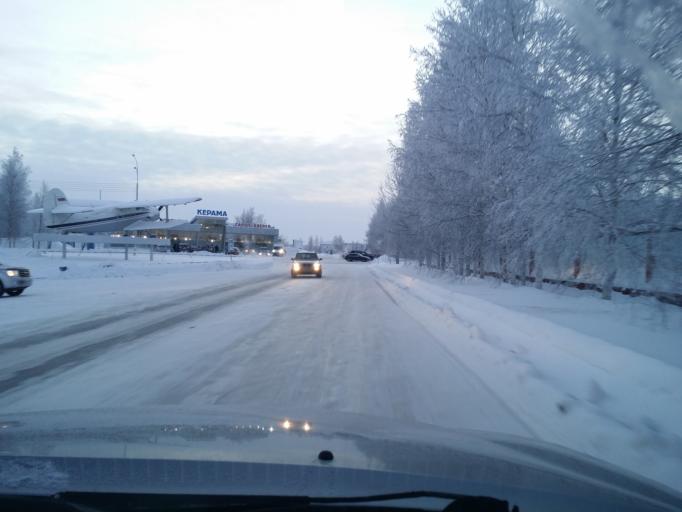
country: RU
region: Khanty-Mansiyskiy Avtonomnyy Okrug
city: Nizhnevartovsk
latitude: 60.9511
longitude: 76.5002
